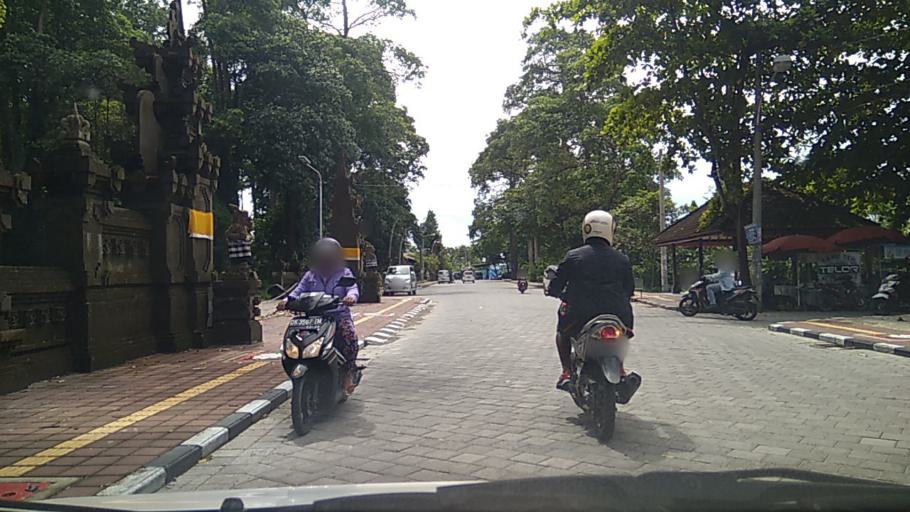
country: ID
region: Bali
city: Dajan Tangluk
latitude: -8.6486
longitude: 115.2468
